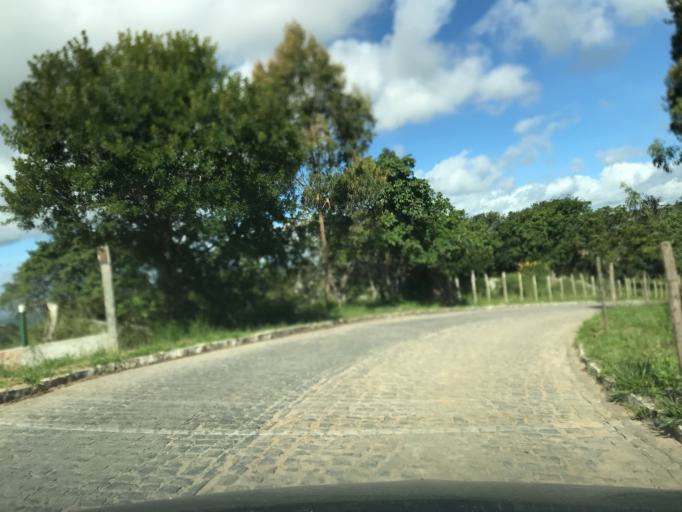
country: BR
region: Pernambuco
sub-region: Bezerros
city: Bezerros
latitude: -8.1735
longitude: -35.7697
